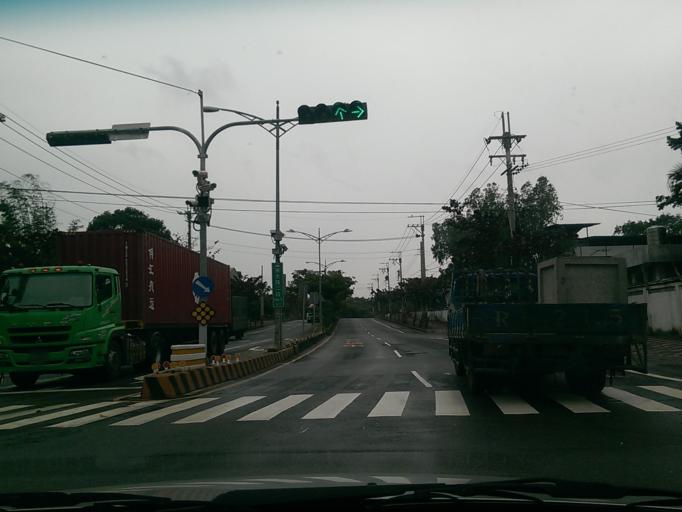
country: TW
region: Taiwan
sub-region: Taichung City
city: Taichung
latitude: 24.2201
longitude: 120.6154
